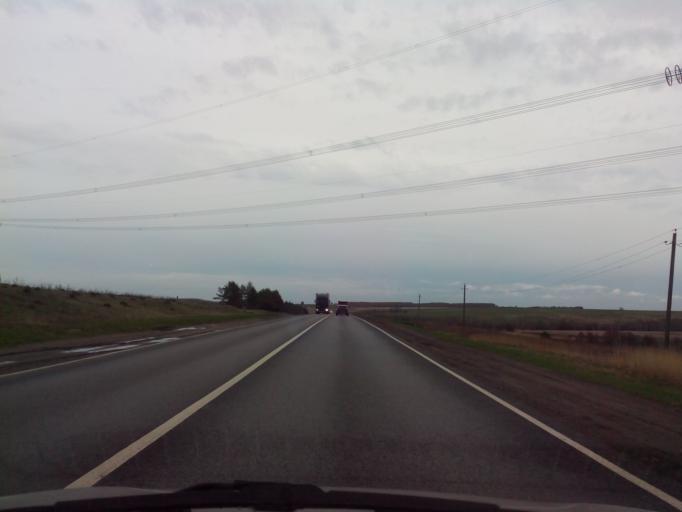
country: RU
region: Moskovskaya
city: Ozherel'ye
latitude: 54.7270
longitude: 38.2687
